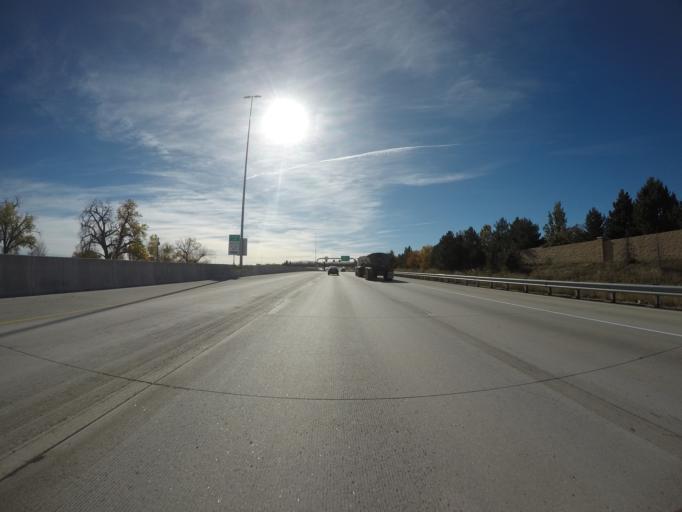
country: US
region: Colorado
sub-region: Adams County
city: Westminster
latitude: 39.8756
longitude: -105.0635
